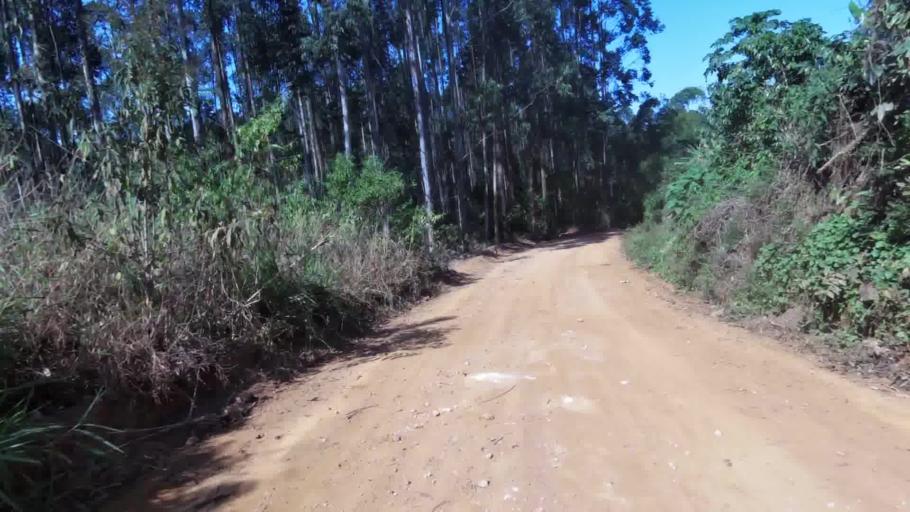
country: BR
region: Espirito Santo
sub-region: Alfredo Chaves
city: Alfredo Chaves
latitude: -20.5356
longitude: -40.8484
